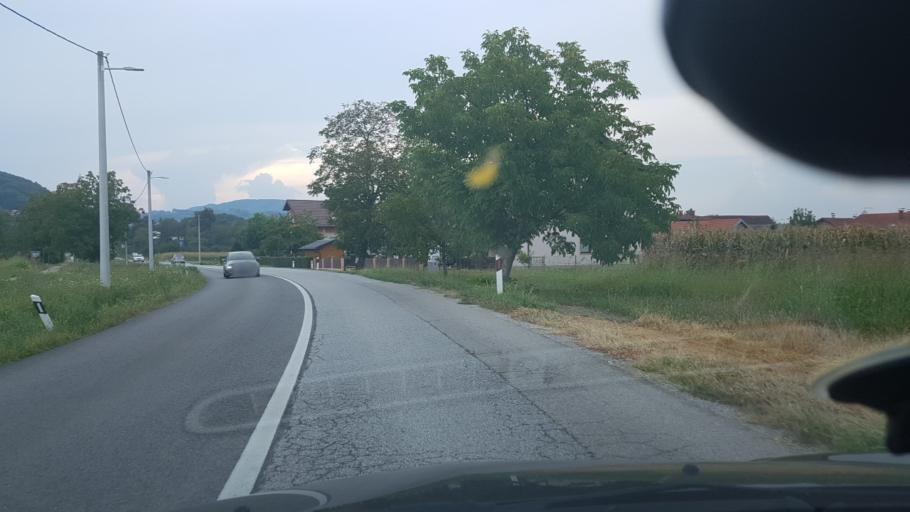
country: HR
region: Zagrebacka
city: Bregana
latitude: 45.8397
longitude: 15.6939
